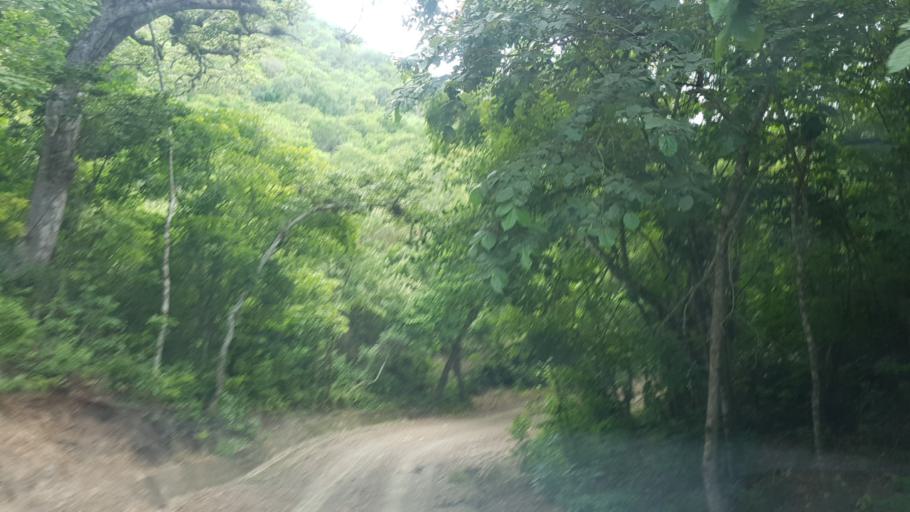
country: NI
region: Nueva Segovia
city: Ocotal
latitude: 13.5997
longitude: -86.4256
